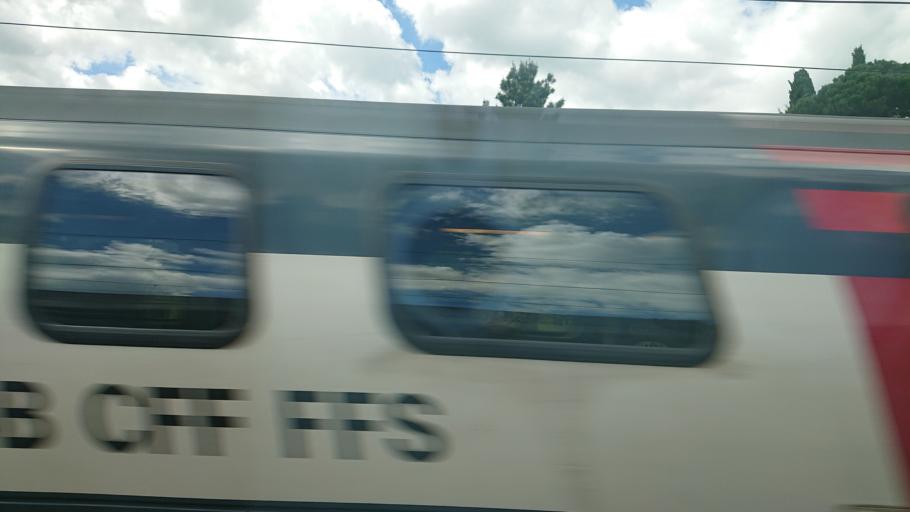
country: CH
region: Vaud
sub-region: Nyon District
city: Coppet
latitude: 46.3064
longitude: 6.1791
